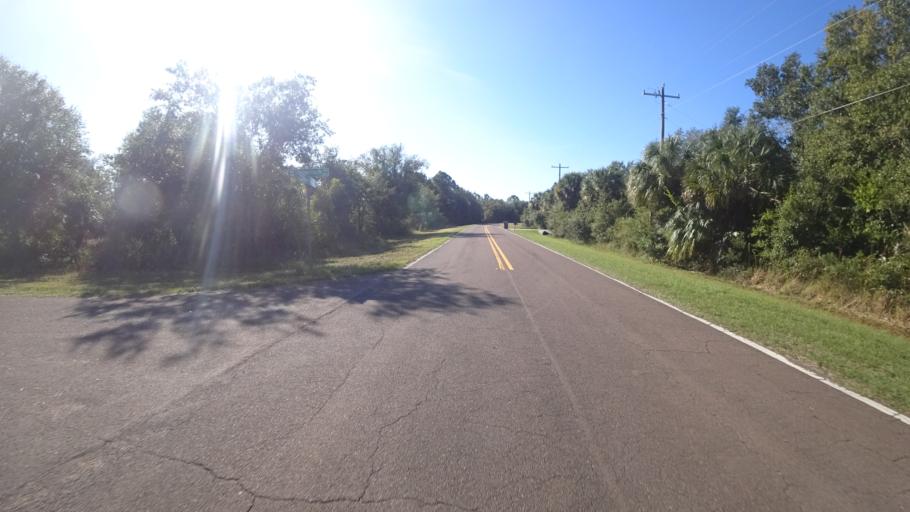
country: US
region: Florida
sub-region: Hillsborough County
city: Sun City Center
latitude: 27.6529
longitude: -82.3848
